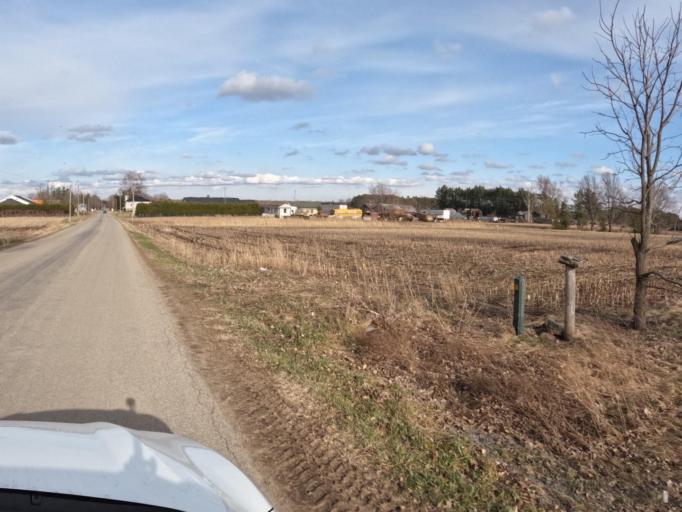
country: CA
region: Ontario
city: Brant
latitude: 42.9972
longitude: -80.4638
